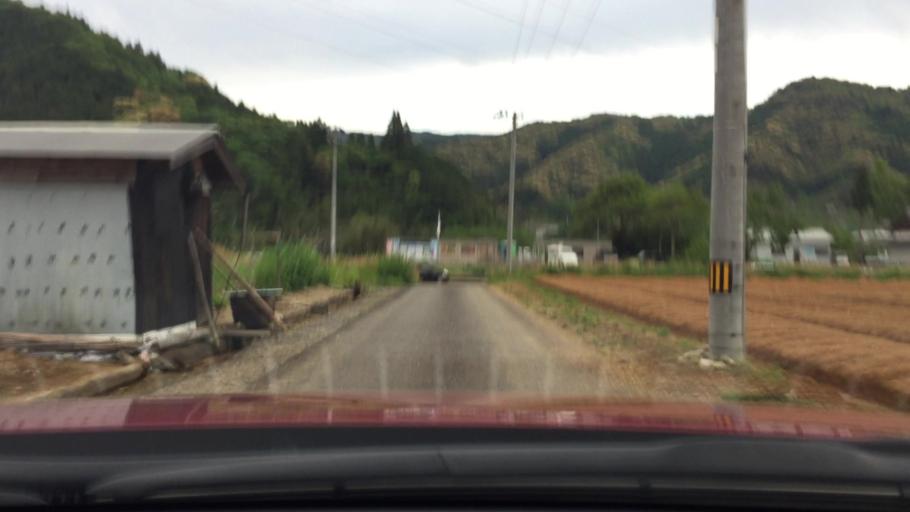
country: JP
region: Kochi
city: Ino
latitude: 33.5272
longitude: 133.3458
